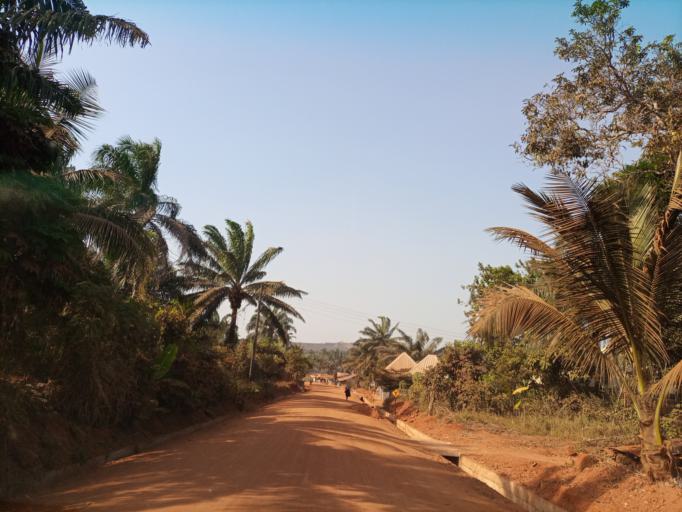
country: NG
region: Enugu
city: Aku
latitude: 6.7008
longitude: 7.3262
